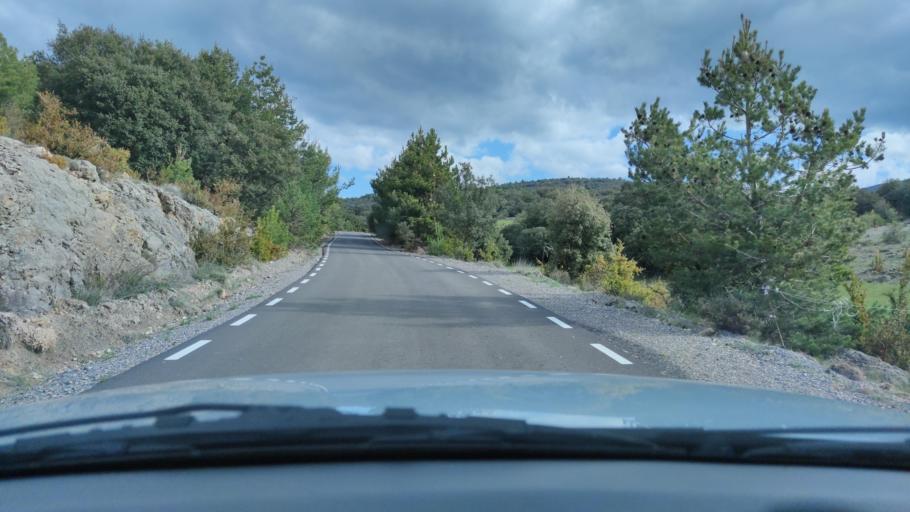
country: ES
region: Catalonia
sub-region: Provincia de Lleida
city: Coll de Nargo
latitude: 42.2357
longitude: 1.4045
